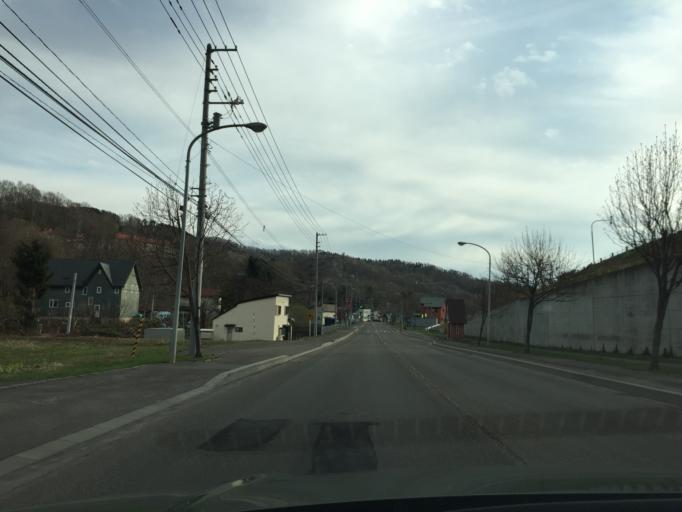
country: JP
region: Hokkaido
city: Utashinai
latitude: 43.5118
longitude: 142.0264
